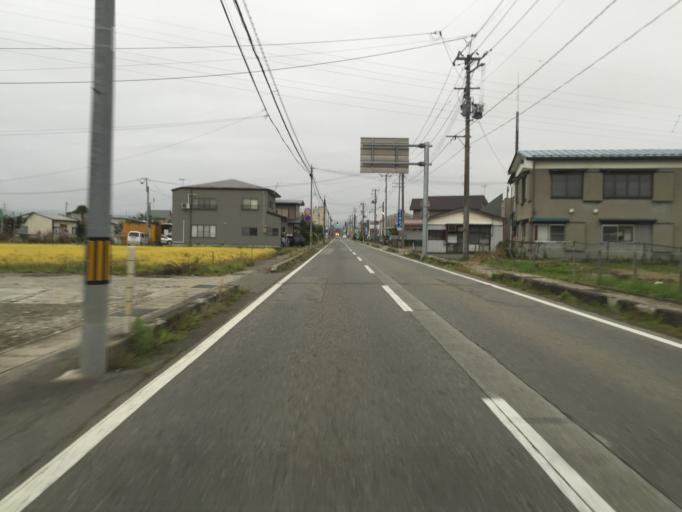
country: JP
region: Fukushima
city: Kitakata
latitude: 37.5134
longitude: 139.9040
